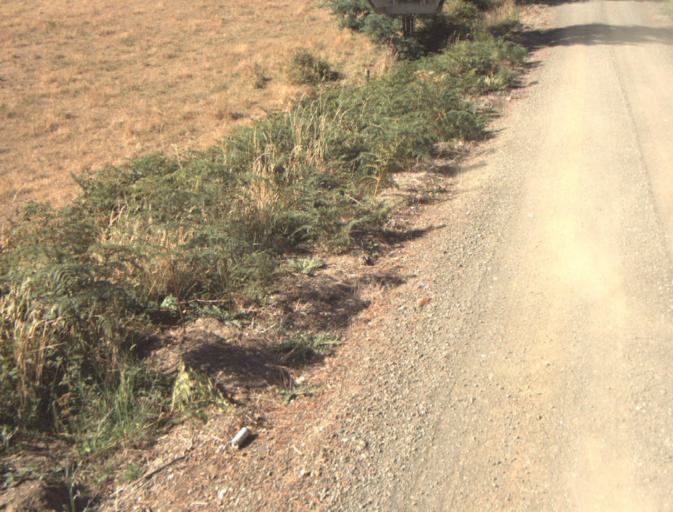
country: AU
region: Tasmania
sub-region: Launceston
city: Mayfield
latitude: -41.1683
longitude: 147.2116
